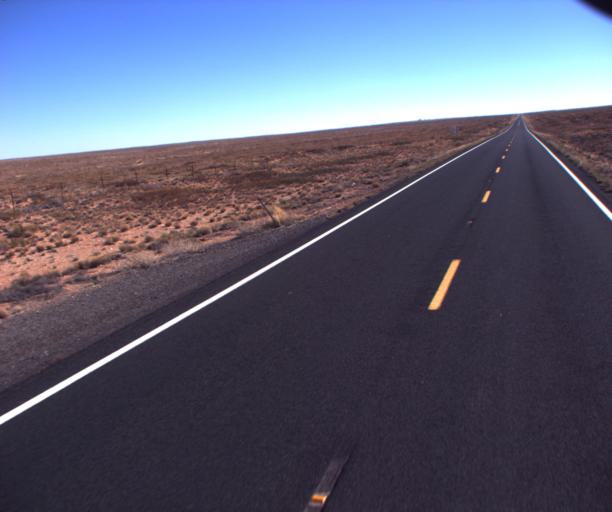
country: US
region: Arizona
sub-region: Coconino County
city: Tuba City
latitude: 36.0188
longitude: -111.1116
